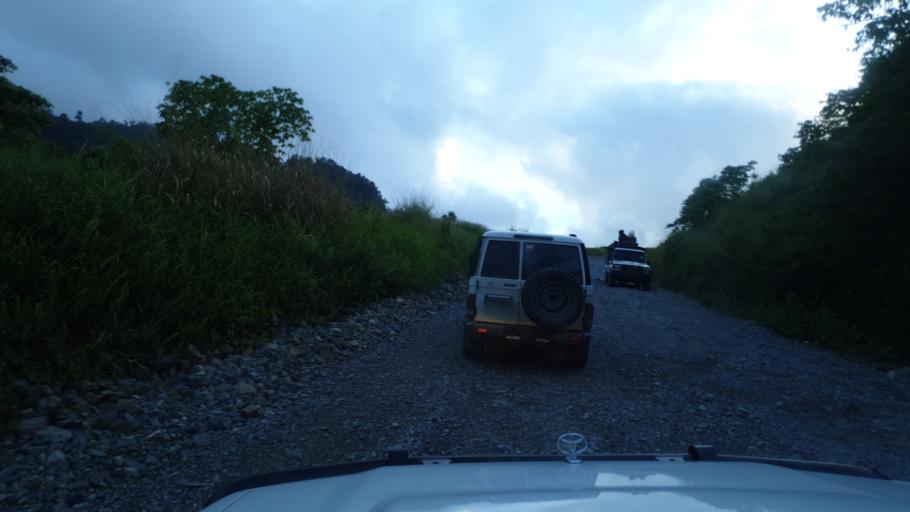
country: PG
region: Bougainville
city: Panguna
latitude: -6.3342
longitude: 155.4646
